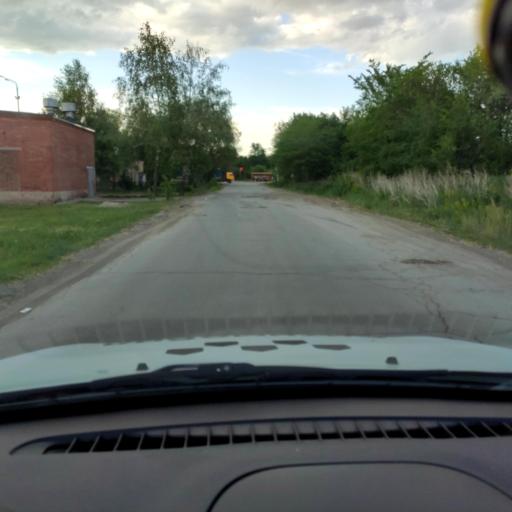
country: RU
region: Samara
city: Podstepki
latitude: 53.5827
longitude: 49.2294
